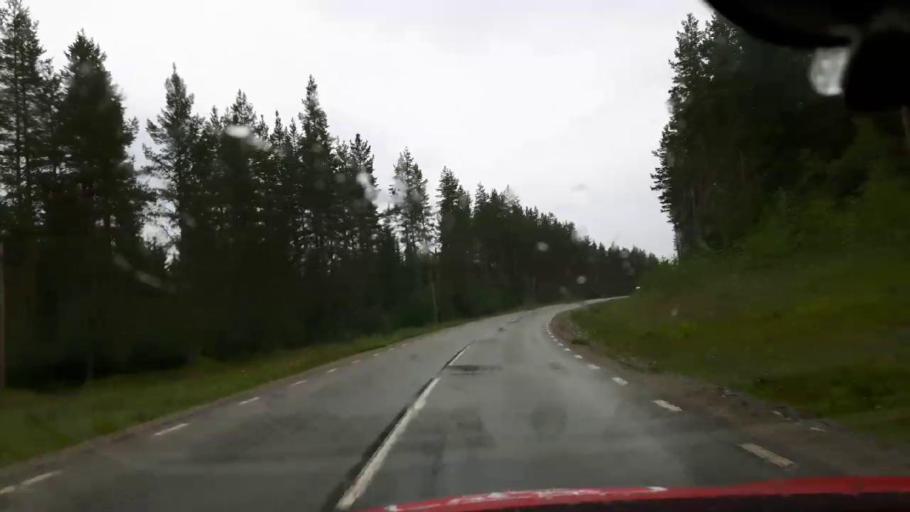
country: SE
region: Jaemtland
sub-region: OEstersunds Kommun
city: Brunflo
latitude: 62.8309
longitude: 15.0080
